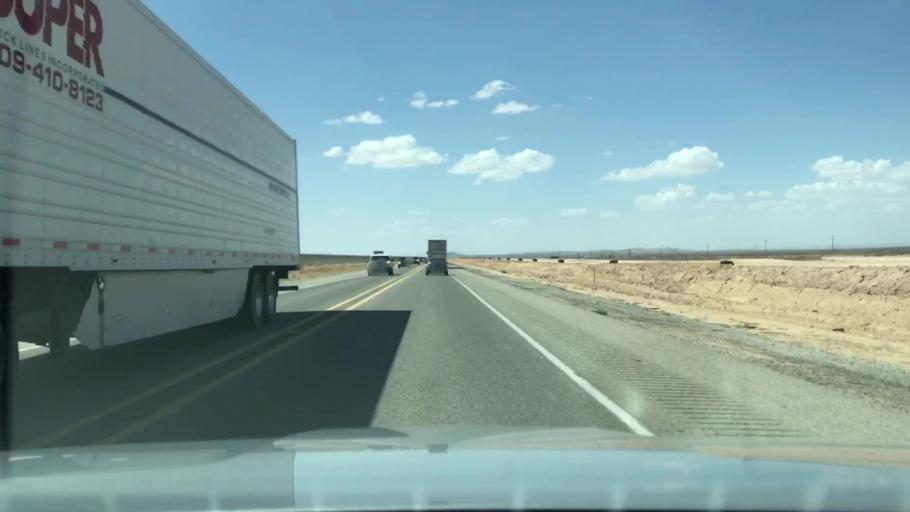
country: US
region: California
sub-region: Kern County
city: Boron
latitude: 34.9659
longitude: -117.4504
